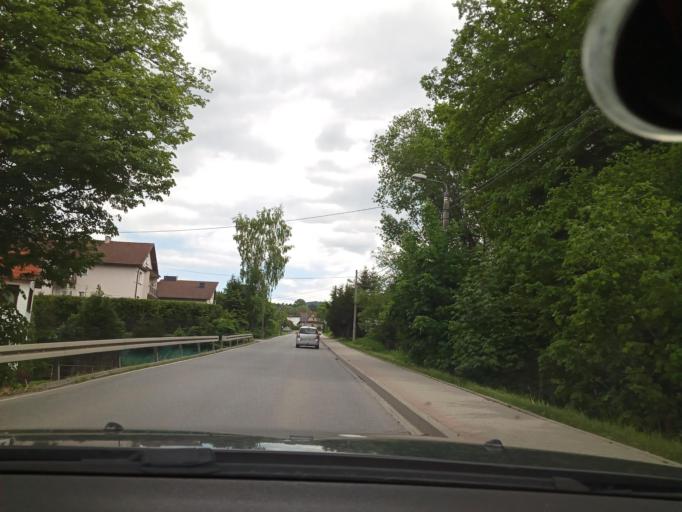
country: PL
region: Lesser Poland Voivodeship
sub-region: Powiat limanowski
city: Limanowa
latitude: 49.7378
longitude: 20.3989
